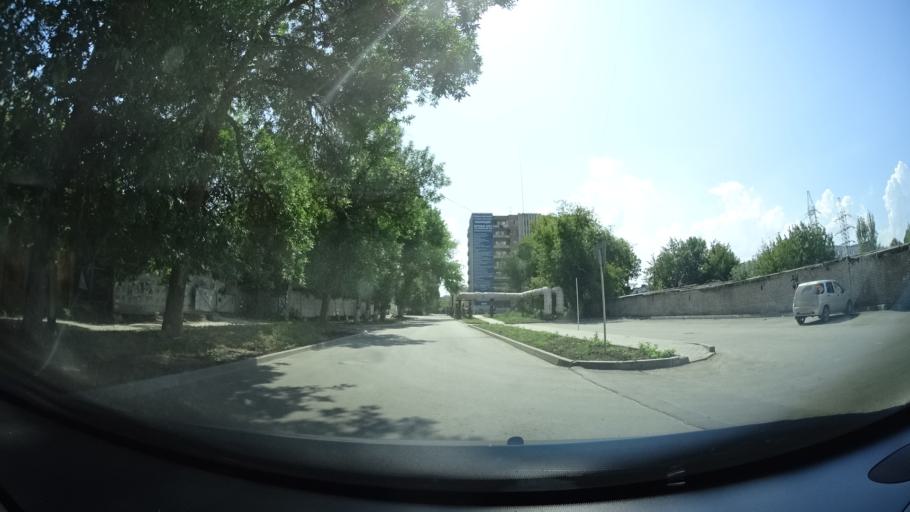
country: RU
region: Samara
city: Samara
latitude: 53.2131
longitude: 50.1487
